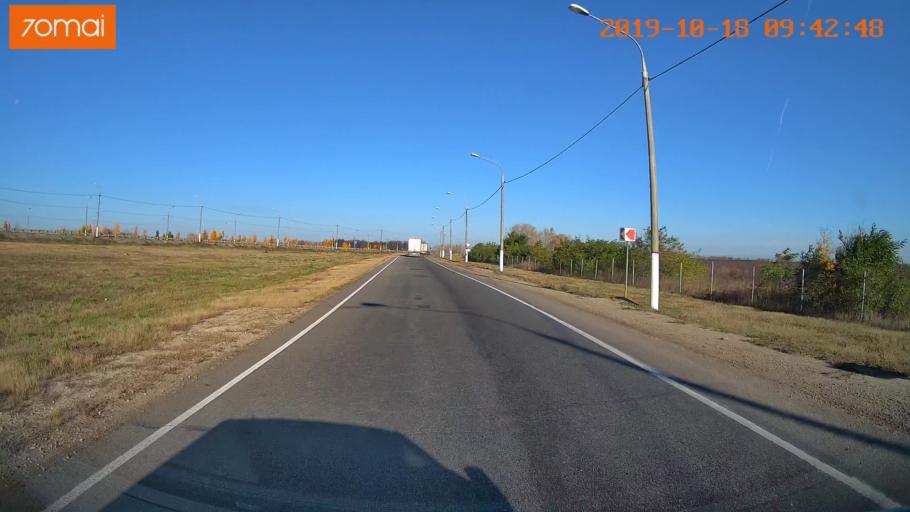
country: RU
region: Tula
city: Kazachka
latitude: 53.2901
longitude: 38.1800
